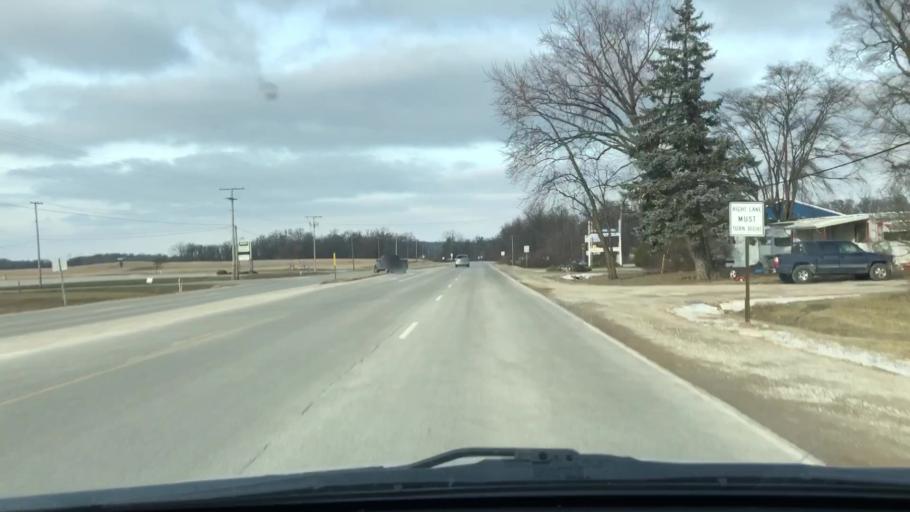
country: US
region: Indiana
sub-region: Steuben County
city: Angola
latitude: 41.6780
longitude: -85.0288
